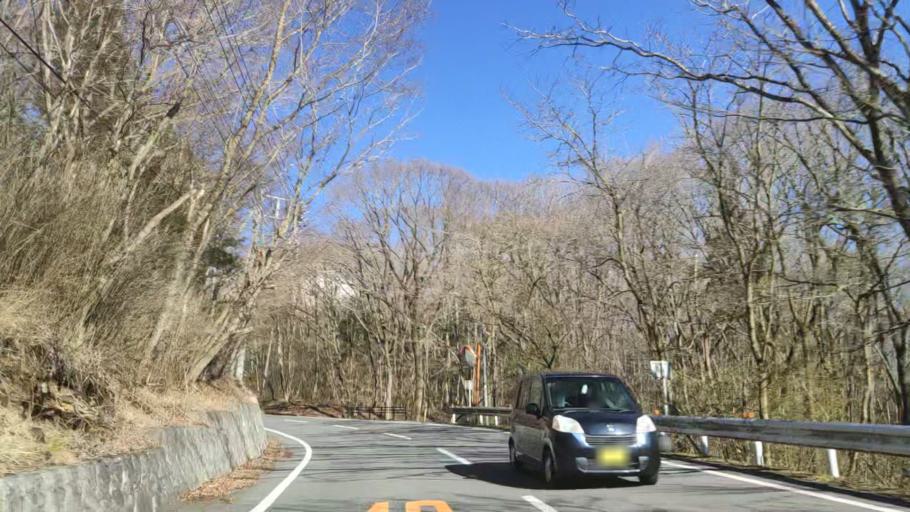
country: JP
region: Shizuoka
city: Fujinomiya
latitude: 35.3587
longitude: 138.6011
